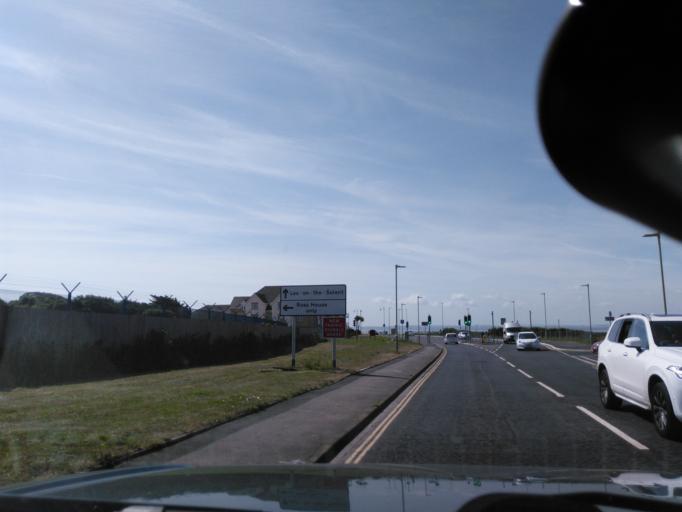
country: GB
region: England
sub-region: Hampshire
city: Lee-on-the-Solent
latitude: 50.8113
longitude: -1.2145
